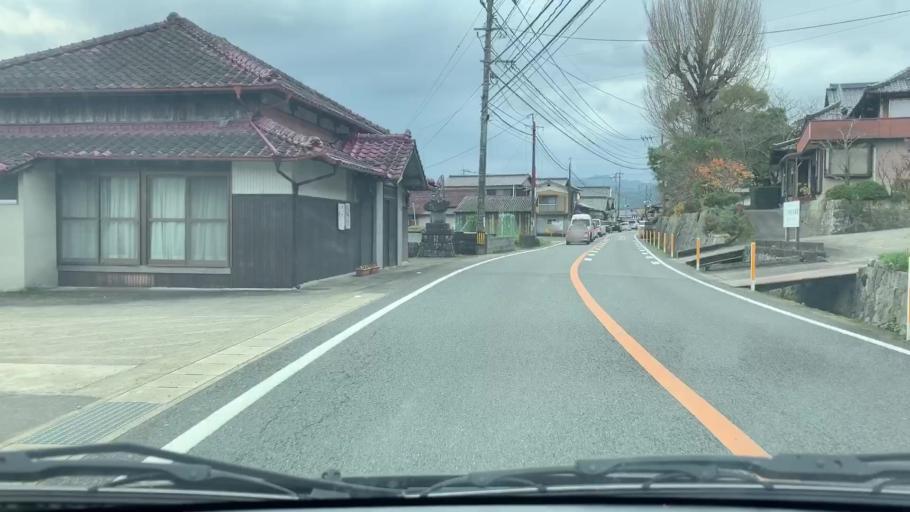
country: JP
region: Saga Prefecture
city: Kashima
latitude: 33.1385
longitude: 130.0639
